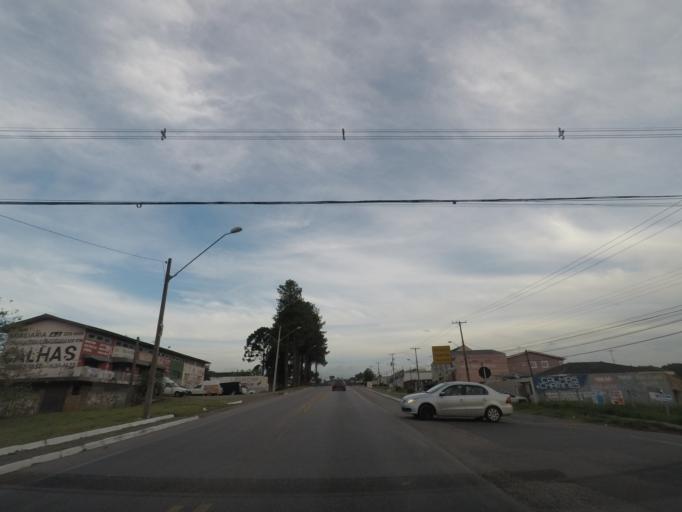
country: BR
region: Parana
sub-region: Colombo
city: Colombo
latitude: -25.3663
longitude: -49.2204
